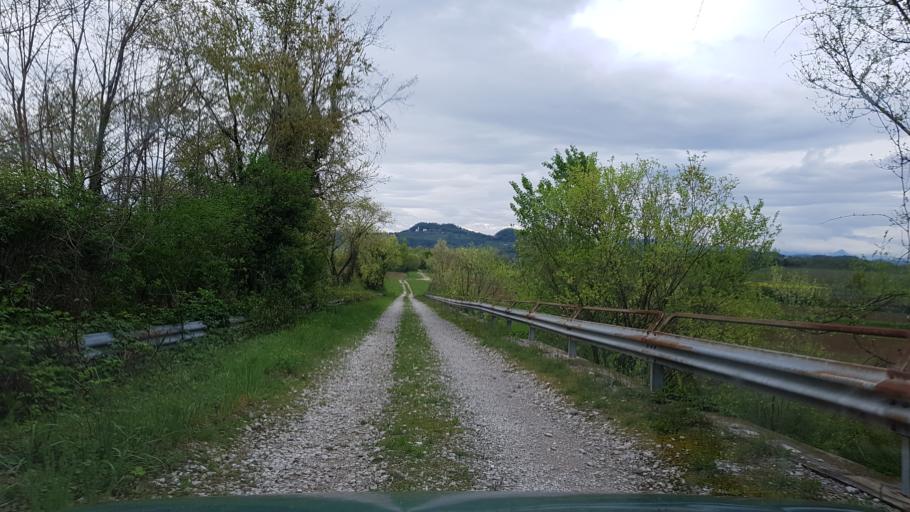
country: IT
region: Friuli Venezia Giulia
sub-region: Provincia di Gorizia
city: Mariano del Friuli
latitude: 45.9304
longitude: 13.4700
